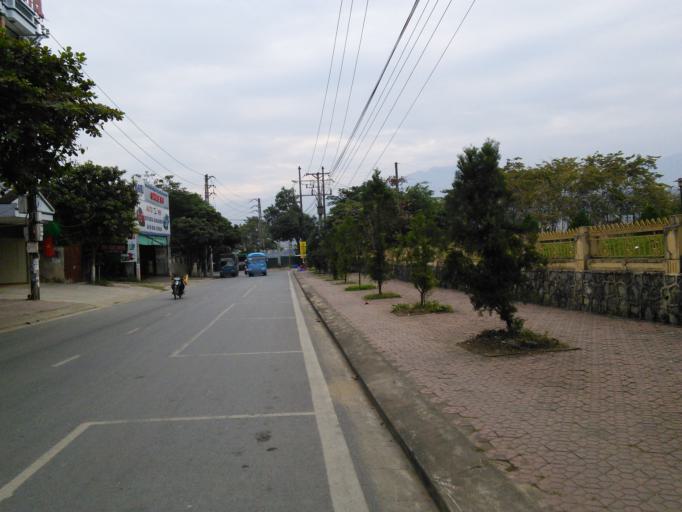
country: VN
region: Lao Cai
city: Lao Cai
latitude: 22.4980
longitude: 103.9724
